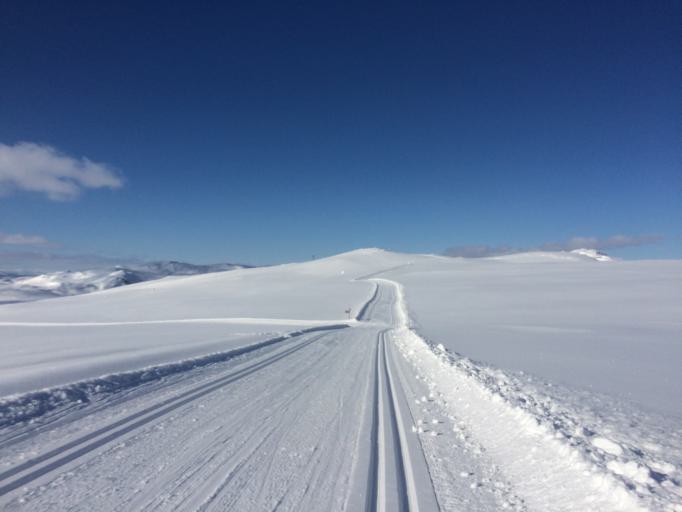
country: NO
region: Oppland
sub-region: Ringebu
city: Ringebu
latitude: 61.3583
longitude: 10.0848
